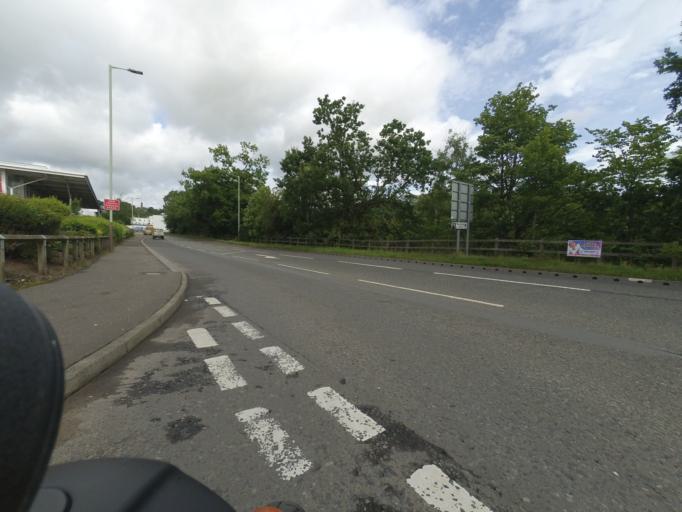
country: GB
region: Scotland
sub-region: Perth and Kinross
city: Blairgowrie
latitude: 56.5895
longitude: -3.3339
